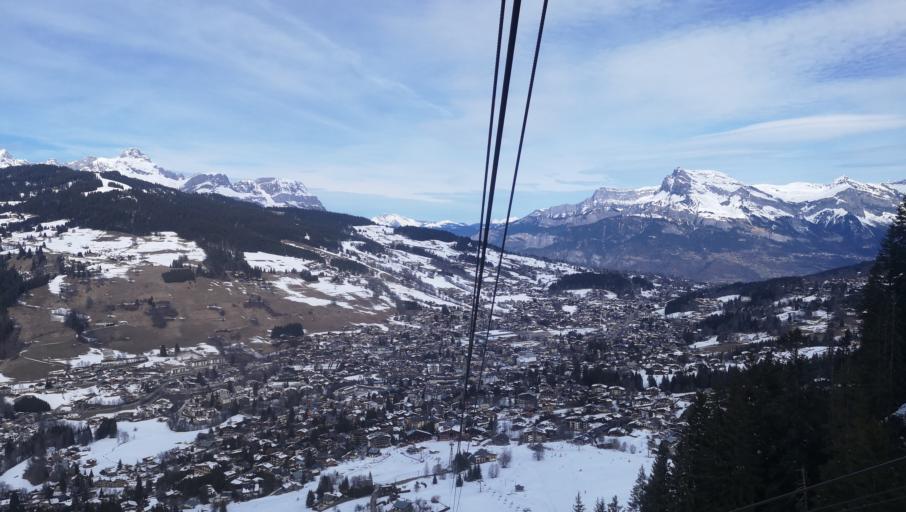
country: FR
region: Rhone-Alpes
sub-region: Departement de la Haute-Savoie
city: Megeve
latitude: 45.8409
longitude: 6.6141
